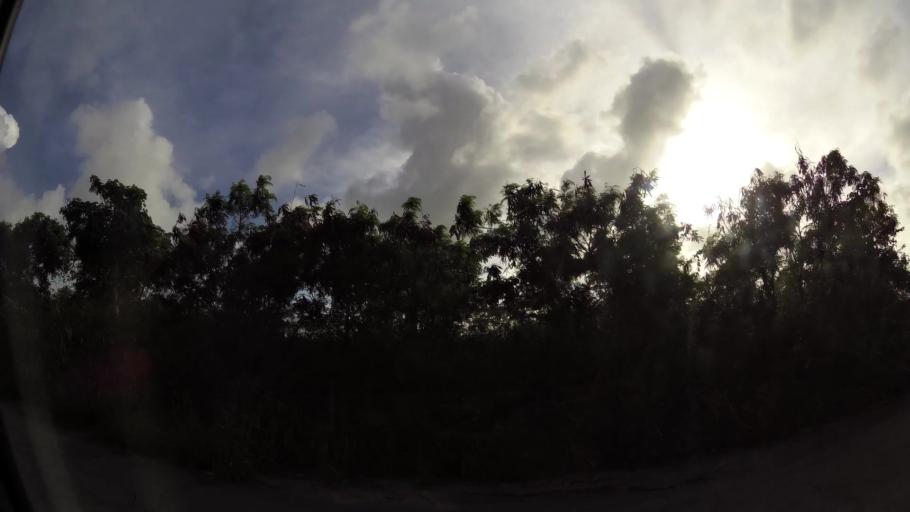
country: BB
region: Christ Church
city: Oistins
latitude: 13.0937
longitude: -59.5512
